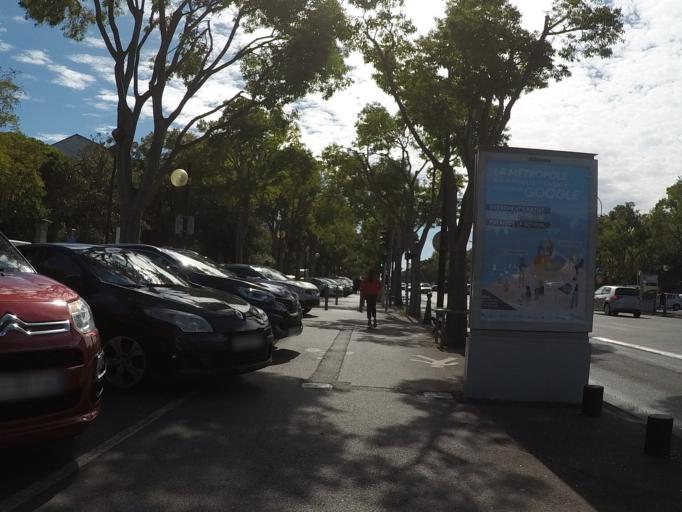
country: FR
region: Provence-Alpes-Cote d'Azur
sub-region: Departement des Bouches-du-Rhone
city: Marseille 08
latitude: 43.2654
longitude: 5.3804
